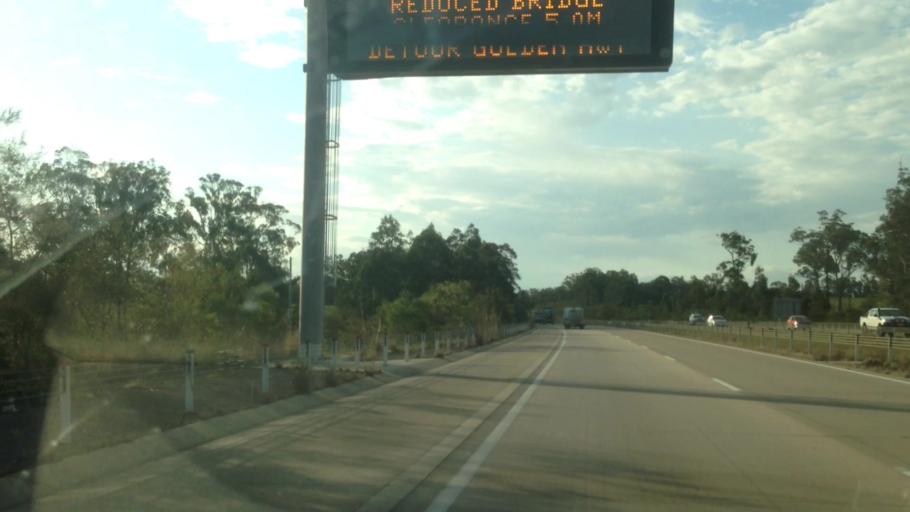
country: AU
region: New South Wales
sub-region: Cessnock
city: Heddon Greta
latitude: -32.8359
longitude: 151.5385
